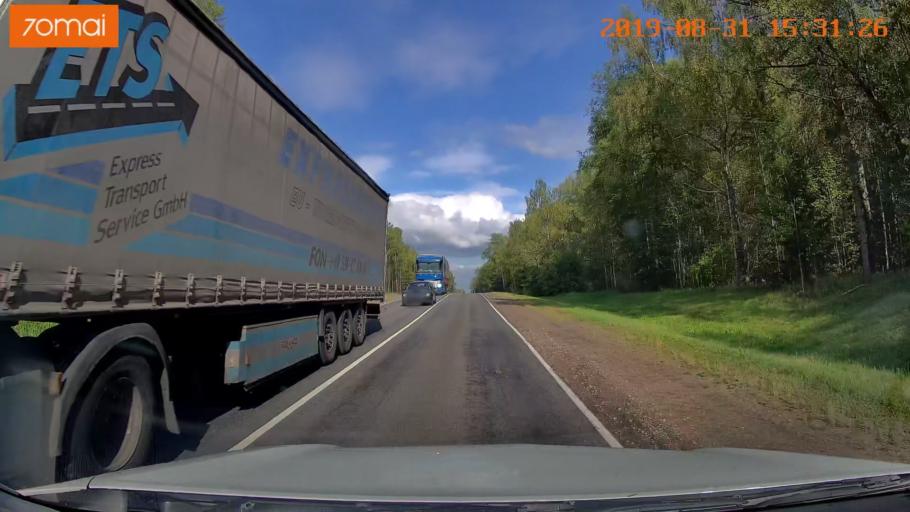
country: RU
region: Kaluga
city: Baryatino
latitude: 54.5825
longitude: 34.6550
